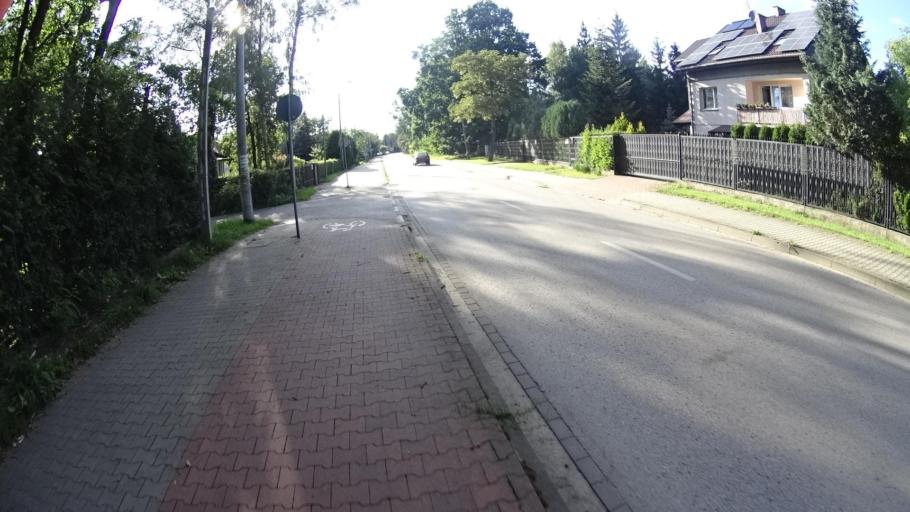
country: PL
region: Masovian Voivodeship
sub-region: Powiat piaseczynski
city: Piaseczno
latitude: 52.0648
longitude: 20.9967
